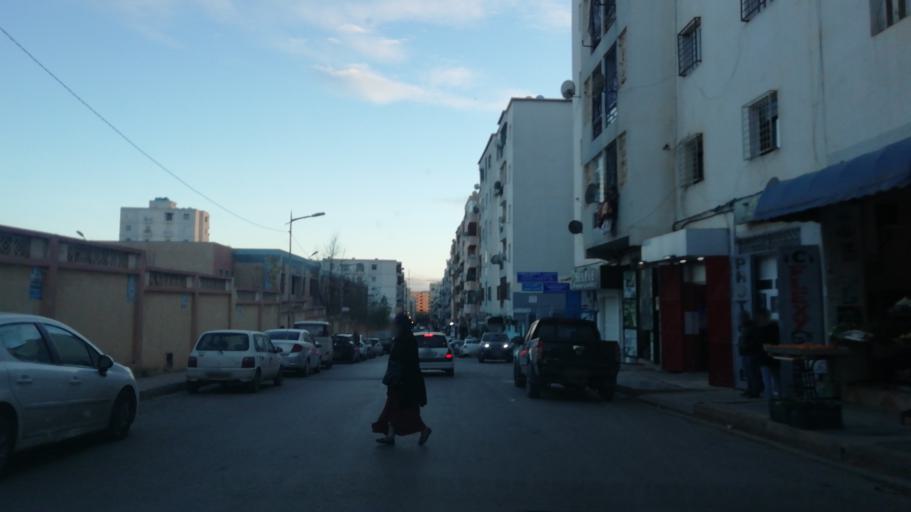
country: DZ
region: Oran
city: Bir el Djir
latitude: 35.7056
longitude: -0.5596
